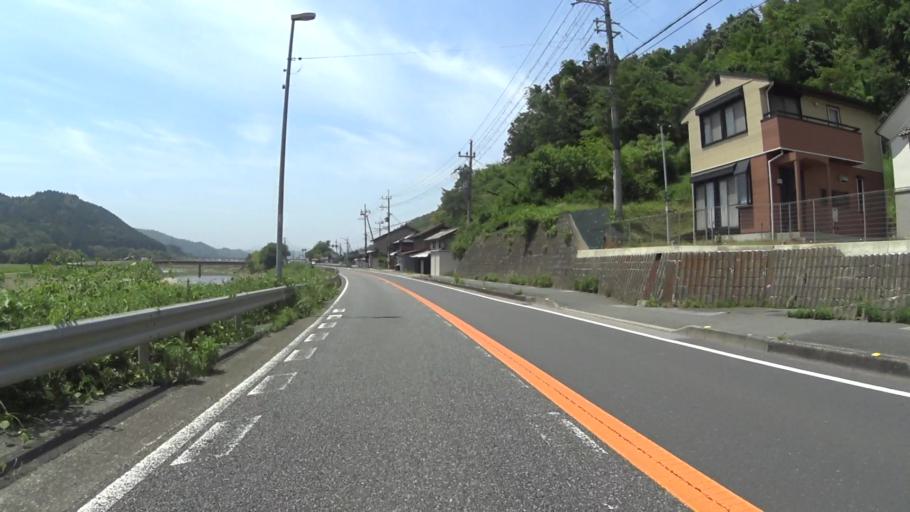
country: JP
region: Kyoto
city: Ayabe
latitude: 35.2551
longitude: 135.2035
